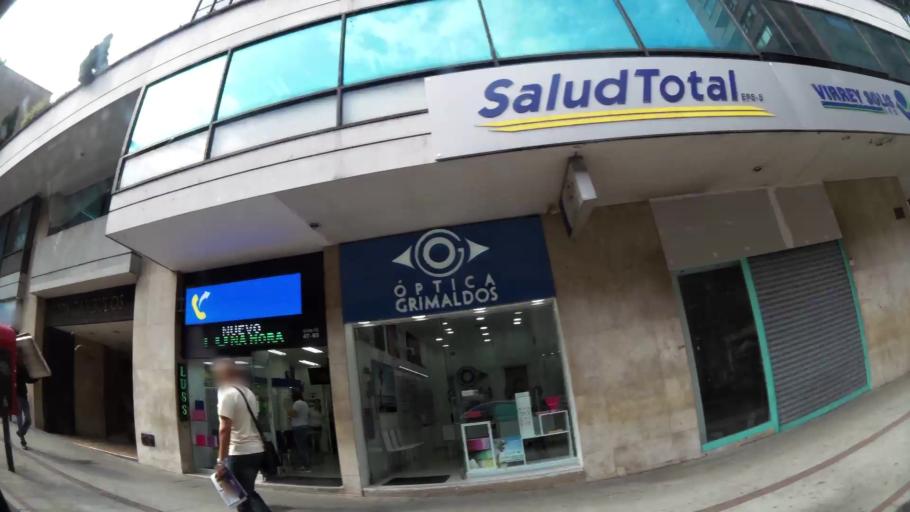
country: CO
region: Antioquia
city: Medellin
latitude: 6.2541
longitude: -75.5663
